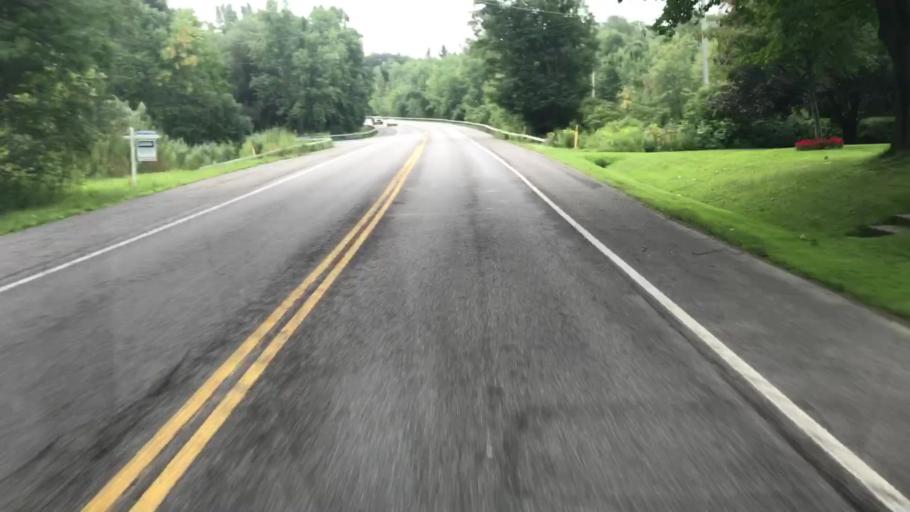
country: US
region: New York
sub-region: Onondaga County
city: Liverpool
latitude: 43.1757
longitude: -76.1993
